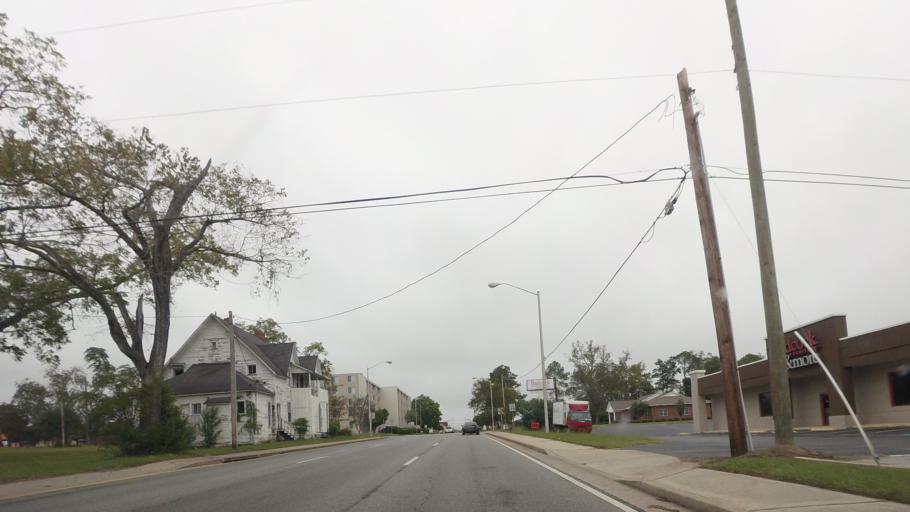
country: US
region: Georgia
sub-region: Ben Hill County
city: Fitzgerald
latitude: 31.7107
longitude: -83.2515
